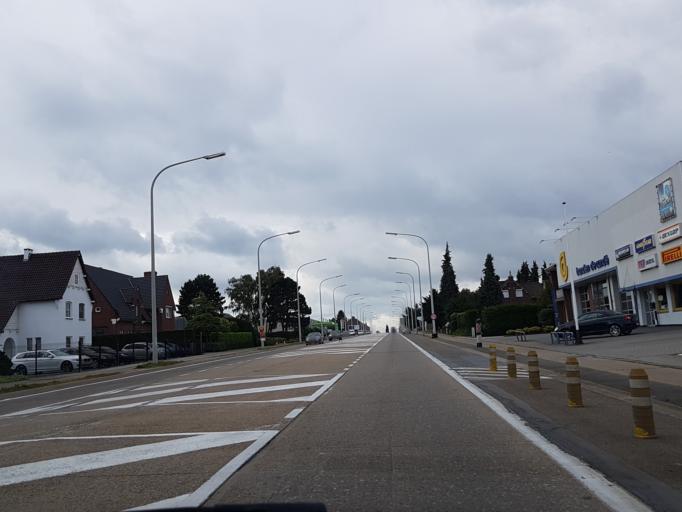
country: BE
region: Flanders
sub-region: Provincie Limburg
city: Sint-Truiden
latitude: 50.8134
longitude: 5.1571
